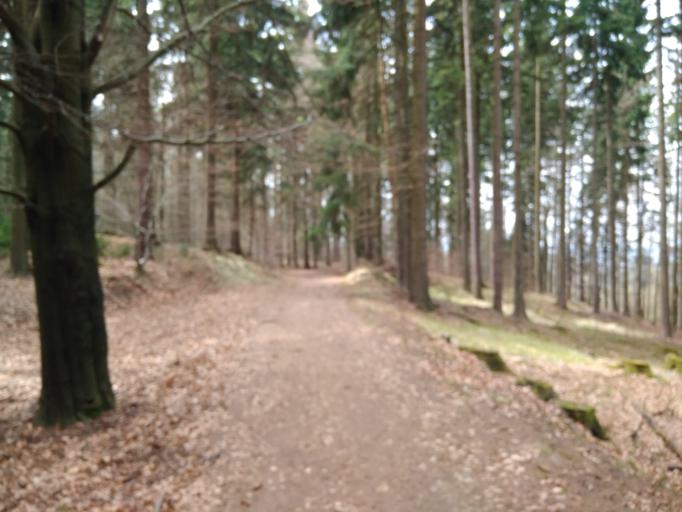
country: CZ
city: Machov
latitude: 50.4633
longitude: 16.2865
